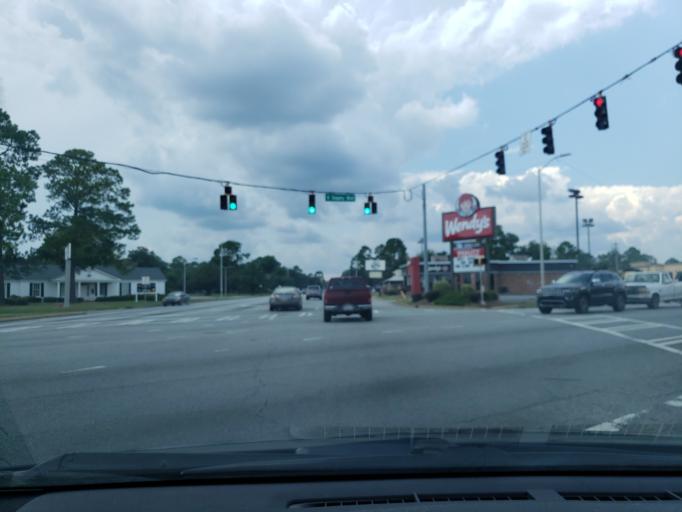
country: US
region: Georgia
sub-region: Dougherty County
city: Albany
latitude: 31.5814
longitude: -84.1760
